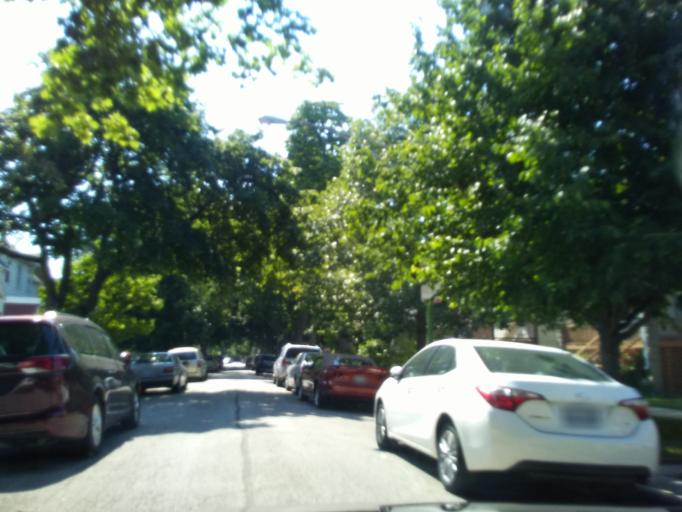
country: US
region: Illinois
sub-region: Cook County
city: Lincolnwood
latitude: 41.9707
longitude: -87.7557
